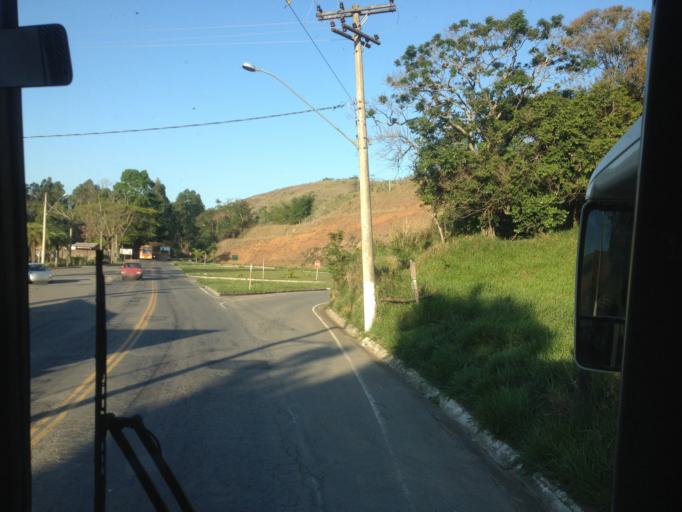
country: BR
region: Minas Gerais
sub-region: Juiz De Fora
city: Juiz de Fora
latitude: -21.6784
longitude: -43.3450
